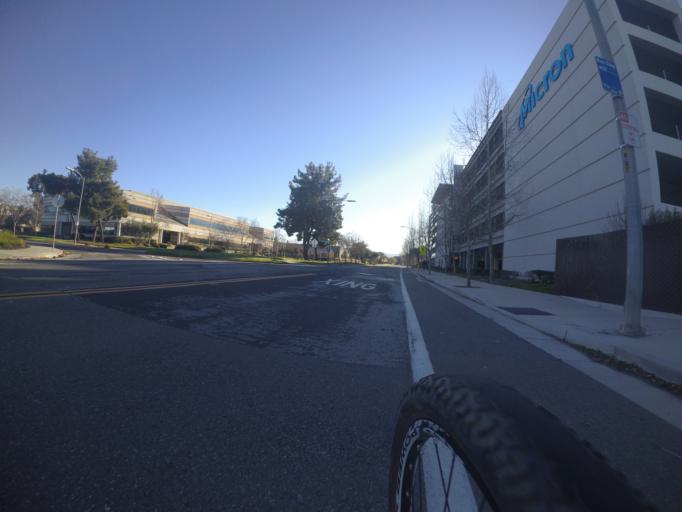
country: US
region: California
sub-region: Santa Clara County
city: Milpitas
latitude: 37.4172
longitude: -121.9508
